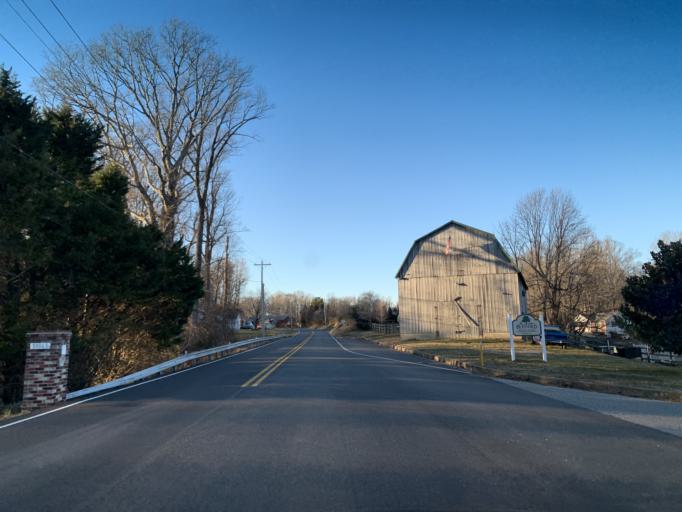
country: US
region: Maryland
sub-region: Saint Mary's County
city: Mechanicsville
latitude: 38.4663
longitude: -76.7247
